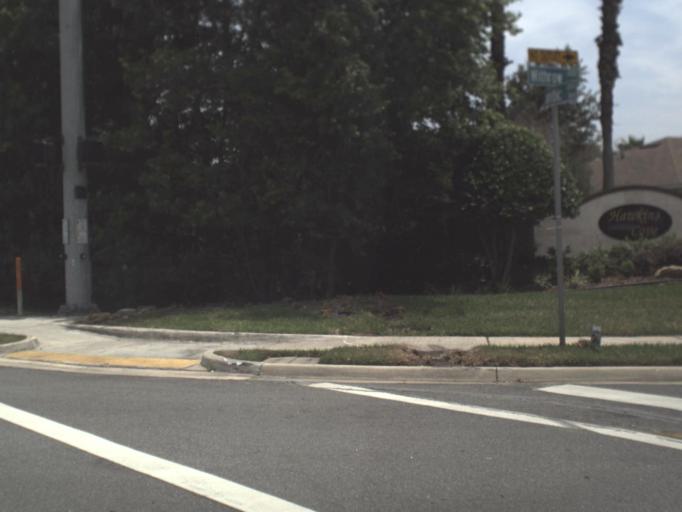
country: US
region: Florida
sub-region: Duval County
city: Atlantic Beach
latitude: 30.3213
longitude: -81.4970
